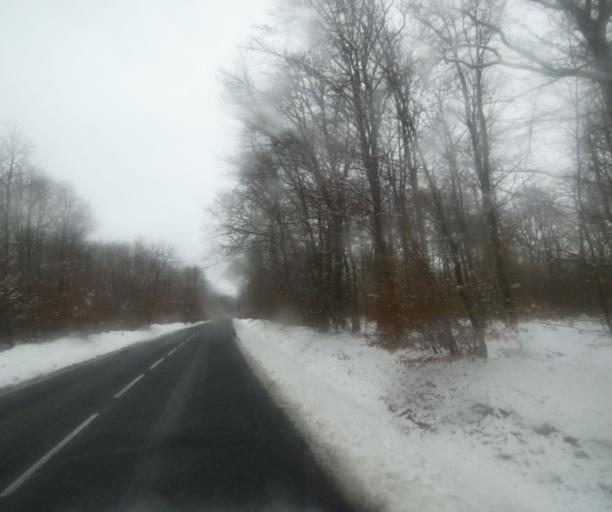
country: FR
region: Champagne-Ardenne
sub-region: Departement de la Haute-Marne
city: Laneuville-a-Remy
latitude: 48.4560
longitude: 4.8790
